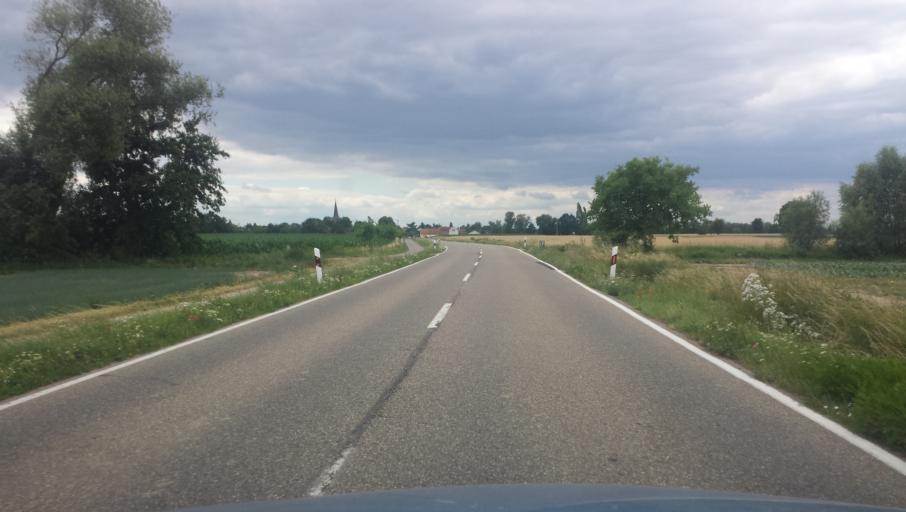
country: DE
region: Rheinland-Pfalz
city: Gommersheim
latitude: 49.2984
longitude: 8.2629
